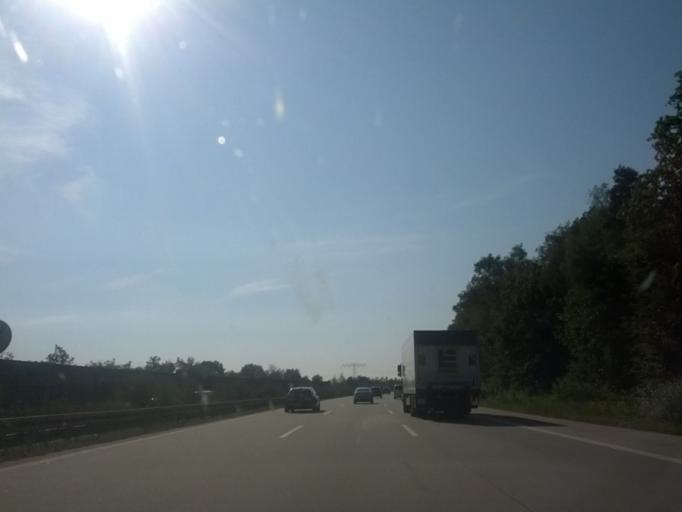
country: DE
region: Brandenburg
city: Woltersdorf
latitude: 52.4603
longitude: 13.7951
